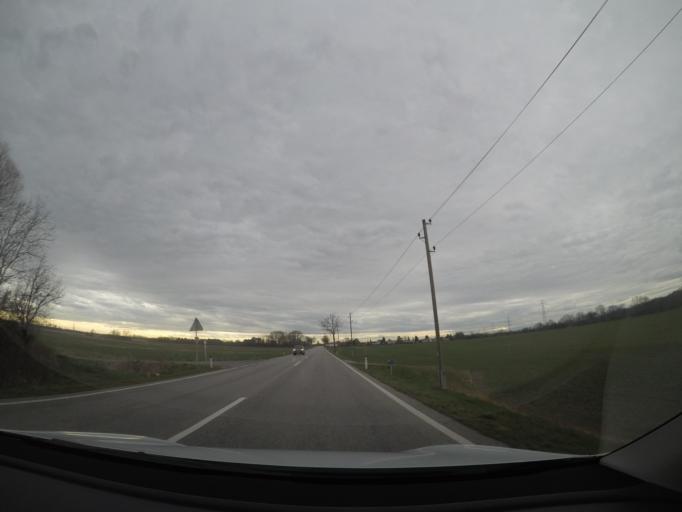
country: AT
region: Lower Austria
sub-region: Politischer Bezirk Modling
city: Achau
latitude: 48.0644
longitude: 16.3820
